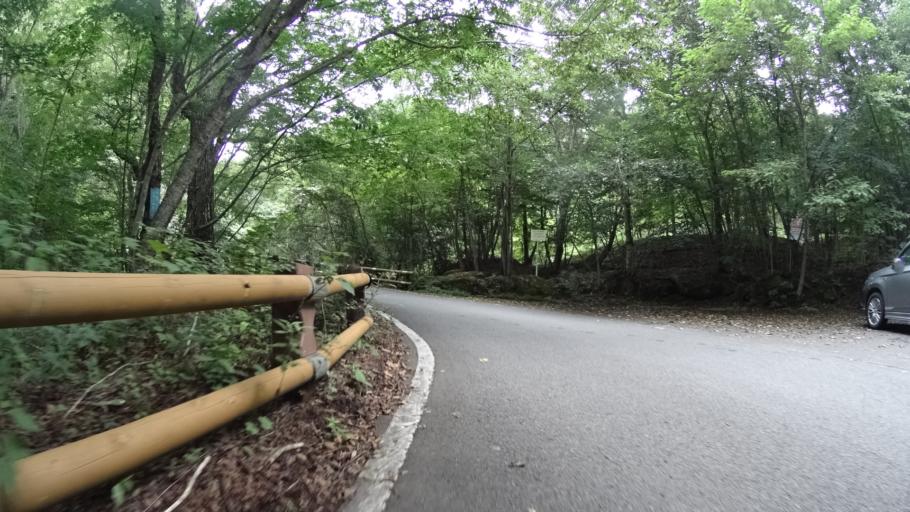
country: JP
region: Yamanashi
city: Kofu-shi
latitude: 35.8581
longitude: 138.5638
